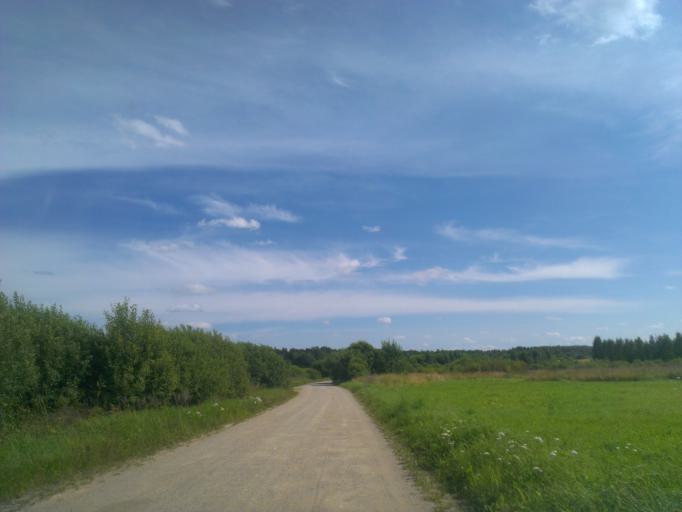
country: LV
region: Ligatne
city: Ligatne
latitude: 57.2223
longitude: 25.0053
